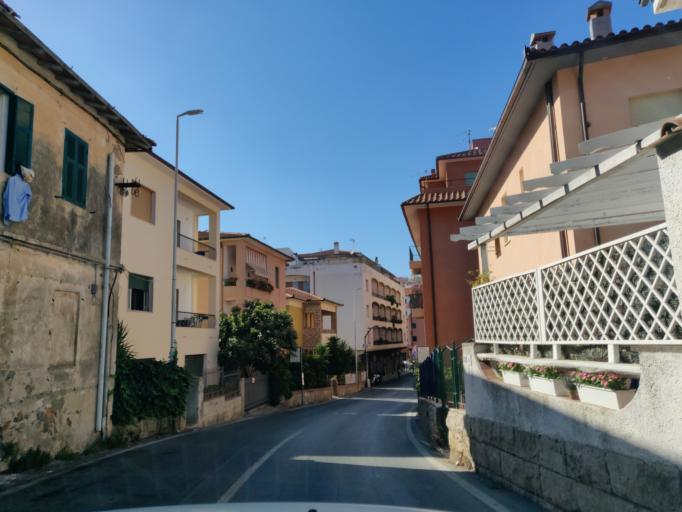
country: IT
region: Tuscany
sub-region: Provincia di Grosseto
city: Porto Ercole
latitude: 42.3927
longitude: 11.2051
